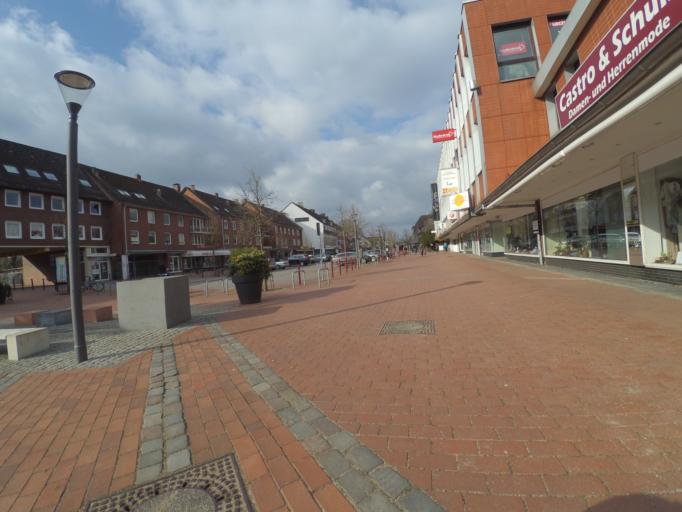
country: DE
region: Hamburg
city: Stellingen
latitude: 53.6184
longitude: 9.9510
